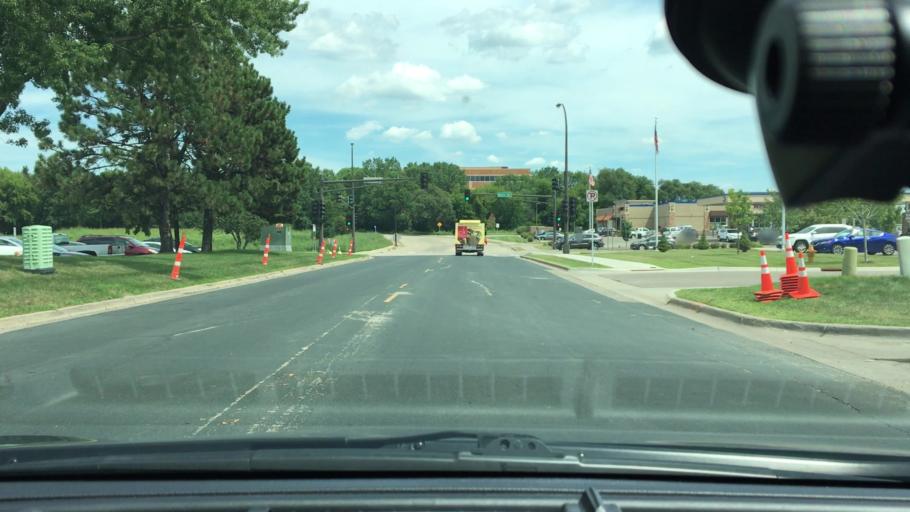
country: US
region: Minnesota
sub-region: Hennepin County
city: Golden Valley
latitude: 44.9857
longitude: -93.3913
